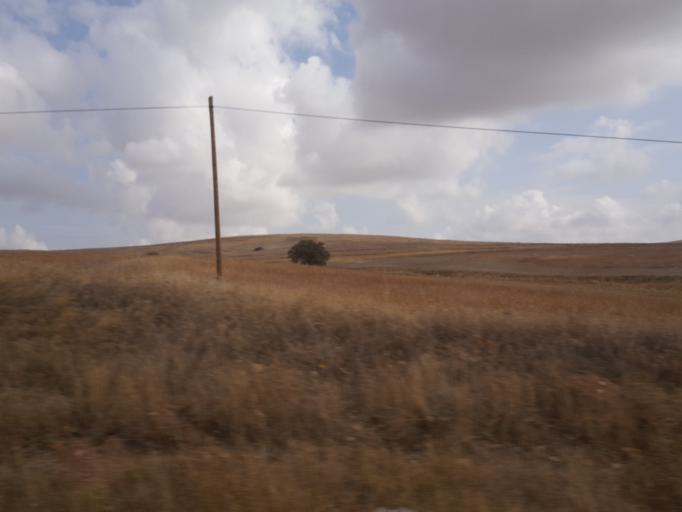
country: TR
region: Kirikkale
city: Keskin
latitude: 39.6358
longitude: 33.6082
